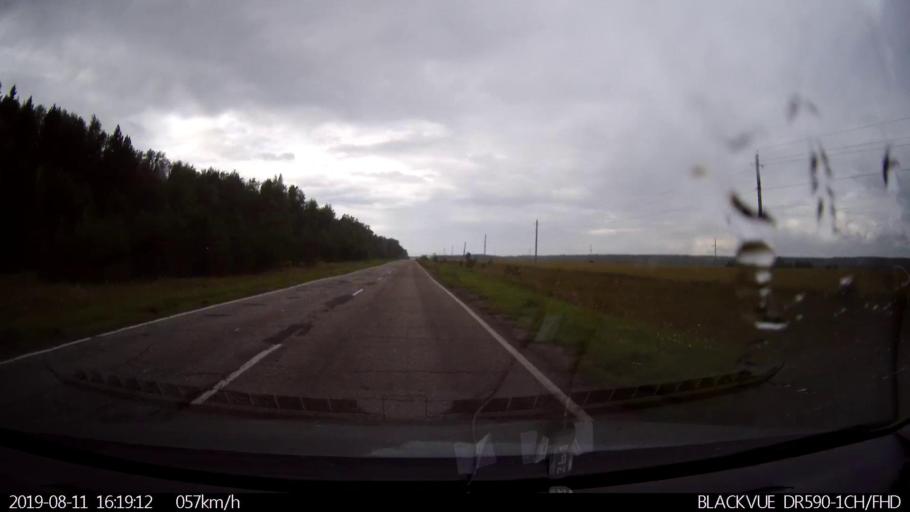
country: RU
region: Ulyanovsk
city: Mayna
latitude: 54.0618
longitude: 47.6085
